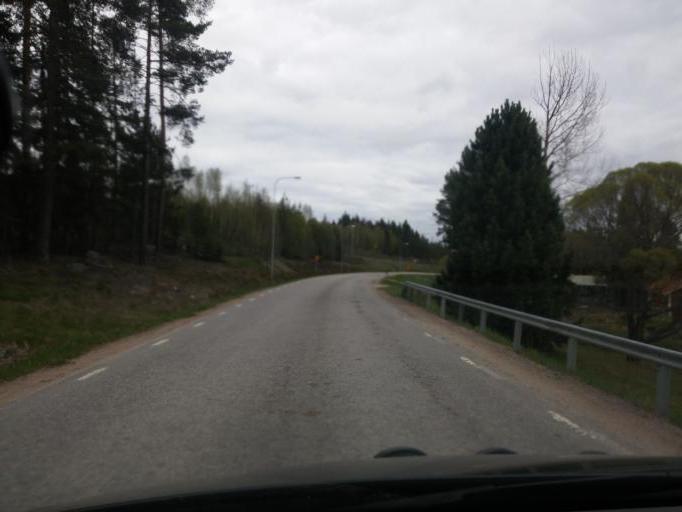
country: SE
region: Gaevleborg
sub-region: Ljusdals Kommun
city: Ljusdal
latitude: 61.8628
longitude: 16.0191
